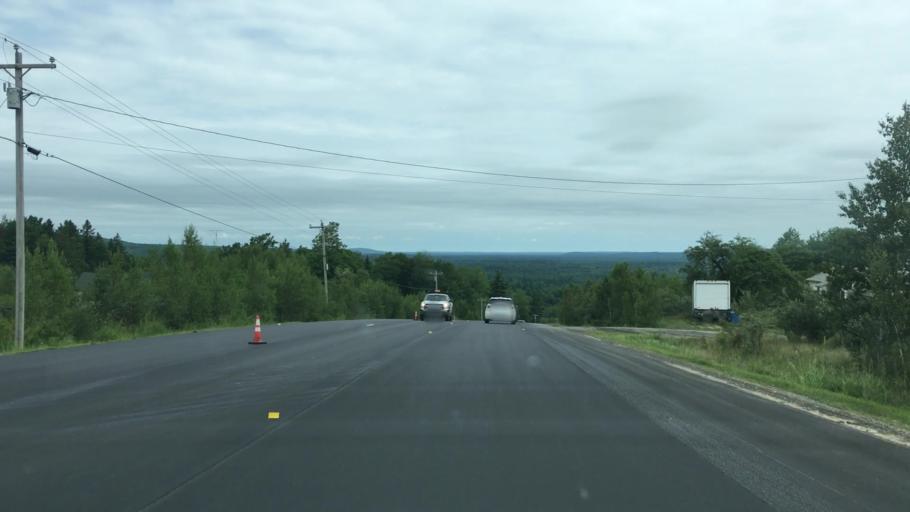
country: US
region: Maine
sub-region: Washington County
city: Machias
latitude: 44.9710
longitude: -67.6465
